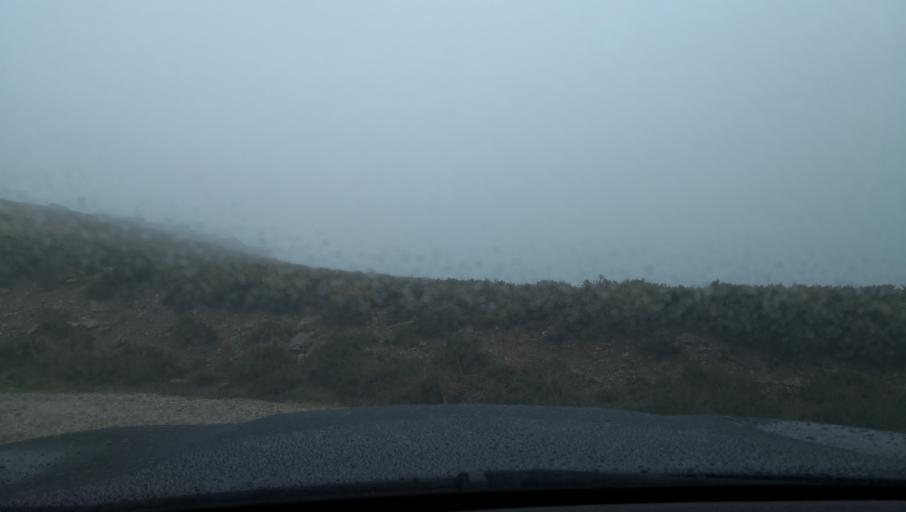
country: PT
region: Vila Real
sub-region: Vila Real
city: Vila Real
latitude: 41.3198
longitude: -7.8329
